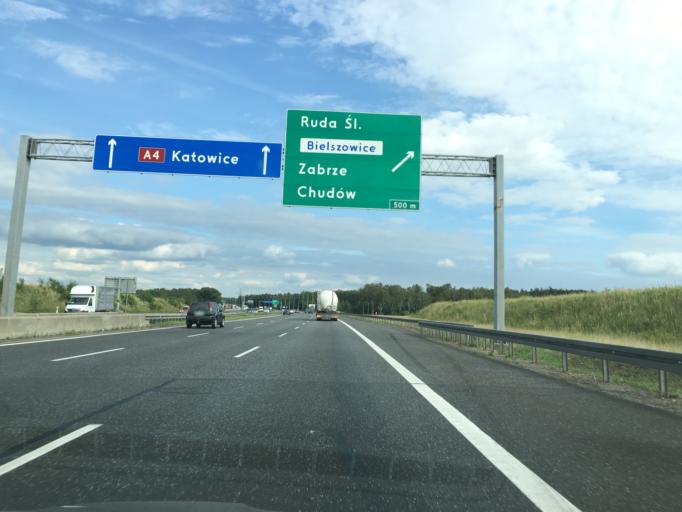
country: PL
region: Silesian Voivodeship
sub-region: Powiat gliwicki
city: Paniowki
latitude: 50.2643
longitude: 18.7816
